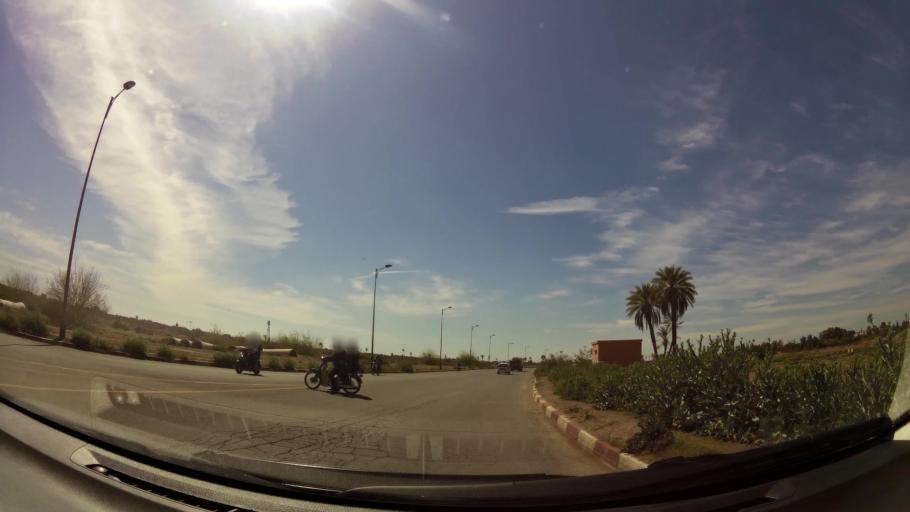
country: MA
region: Marrakech-Tensift-Al Haouz
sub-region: Marrakech
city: Marrakesh
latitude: 31.6170
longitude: -7.9548
